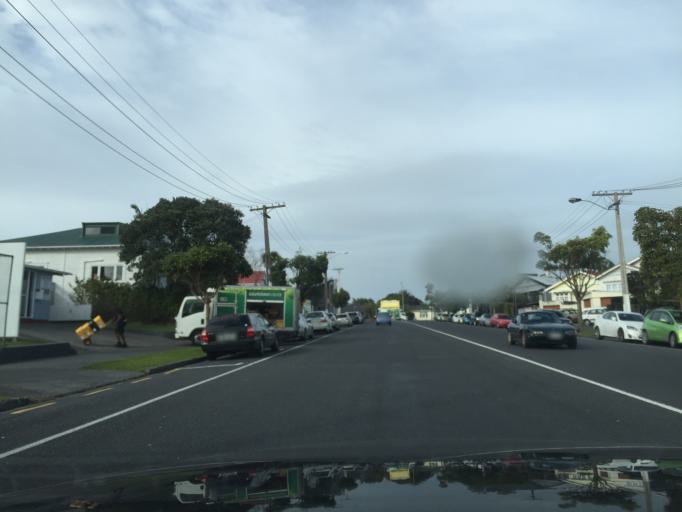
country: NZ
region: Auckland
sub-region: Auckland
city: Auckland
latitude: -36.8608
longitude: 174.7328
